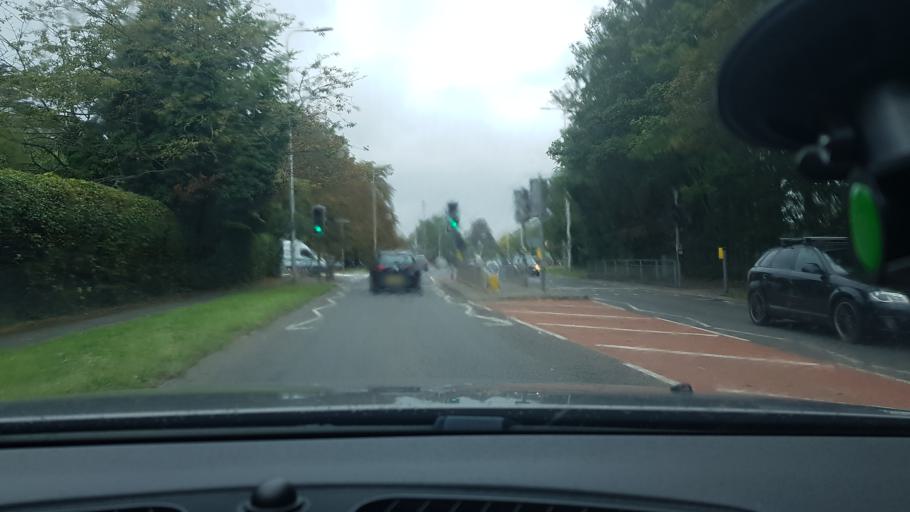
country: GB
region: England
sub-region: West Berkshire
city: Newbury
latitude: 51.4077
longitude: -1.3353
